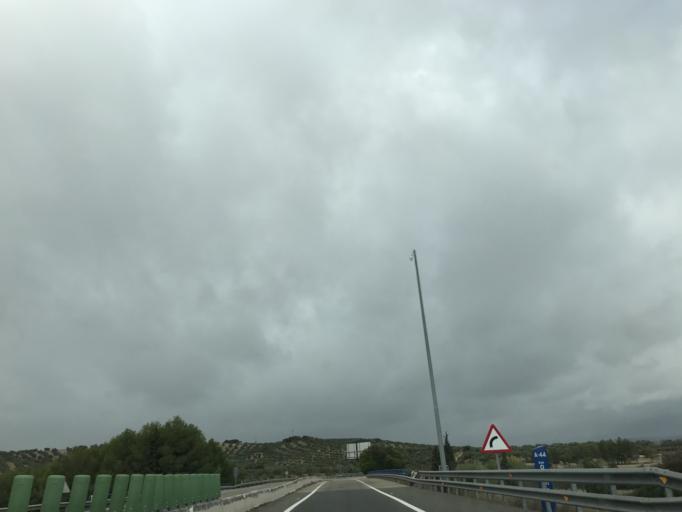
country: ES
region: Andalusia
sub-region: Provincia de Jaen
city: Bailen
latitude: 38.1203
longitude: -3.7601
